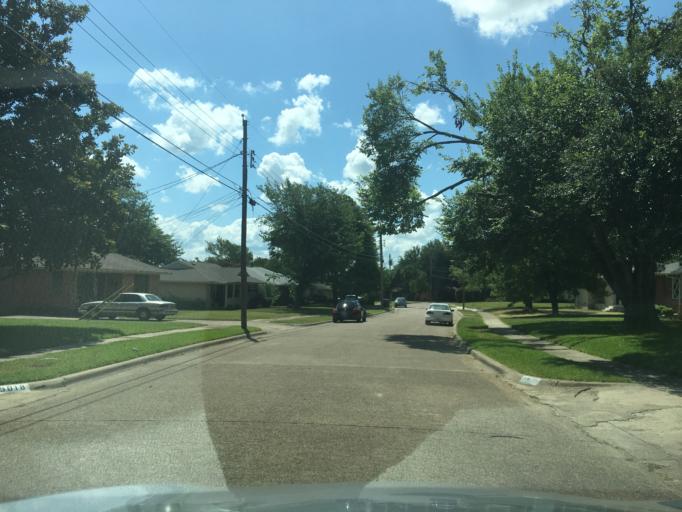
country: US
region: Texas
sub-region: Dallas County
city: Garland
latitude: 32.8709
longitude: -96.7026
